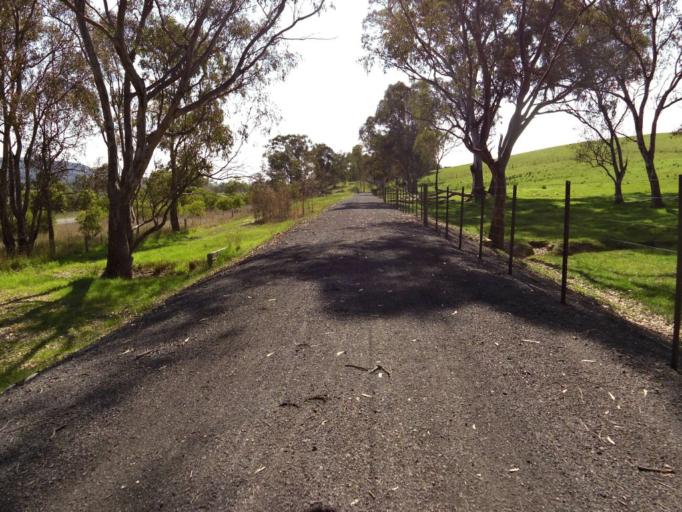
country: AU
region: Victoria
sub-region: Murrindindi
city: Alexandra
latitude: -37.1336
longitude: 145.5929
